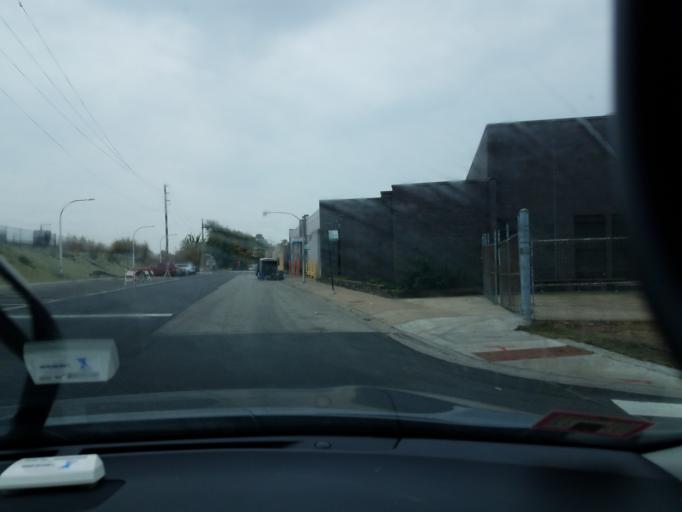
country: US
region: Illinois
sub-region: Cook County
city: Lincolnwood
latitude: 41.9480
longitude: -87.7403
